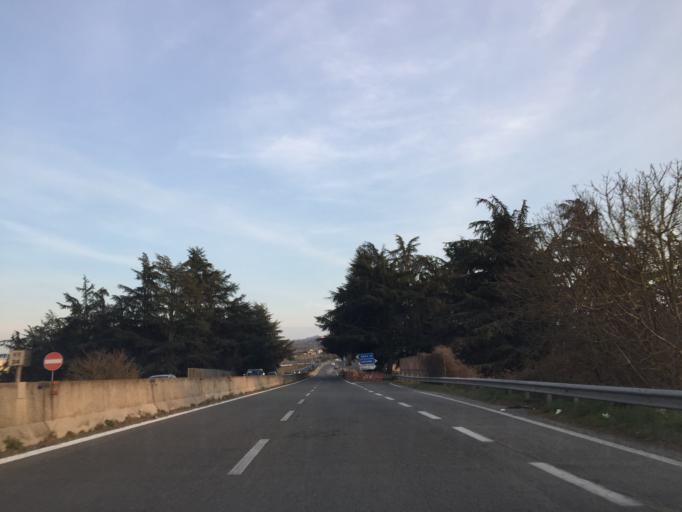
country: IT
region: Latium
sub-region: Citta metropolitana di Roma Capitale
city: Campagnano di Roma
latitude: 42.1552
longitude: 12.3441
